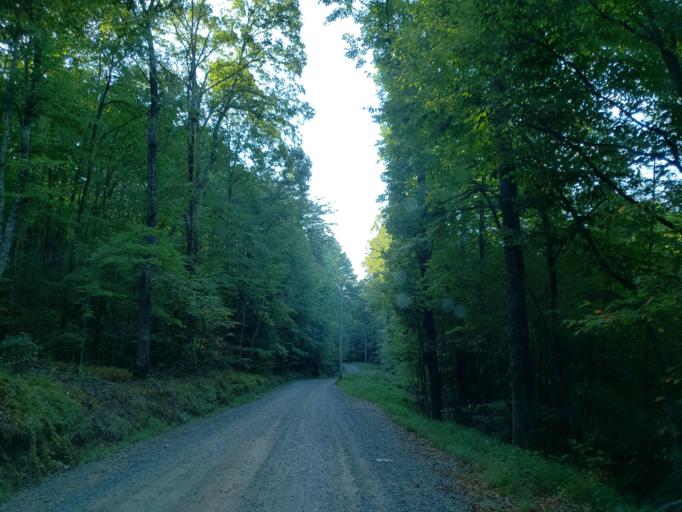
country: US
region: Georgia
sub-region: Fannin County
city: Blue Ridge
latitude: 34.6824
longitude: -84.2637
